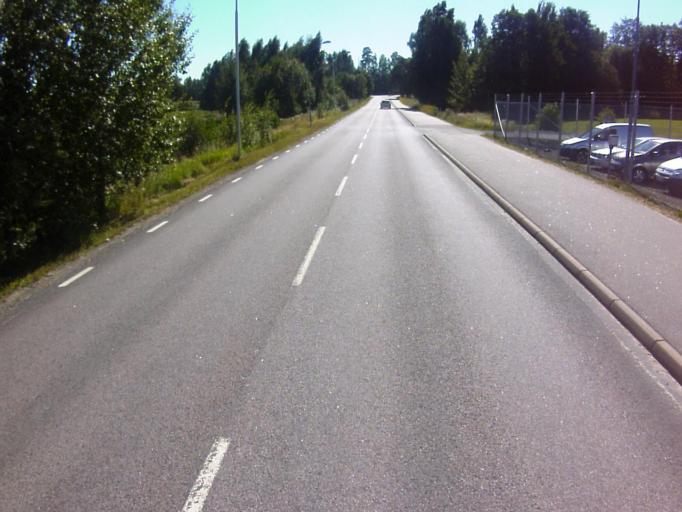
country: SE
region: Soedermanland
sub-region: Eskilstuna Kommun
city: Hallbybrunn
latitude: 59.3826
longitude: 16.4349
